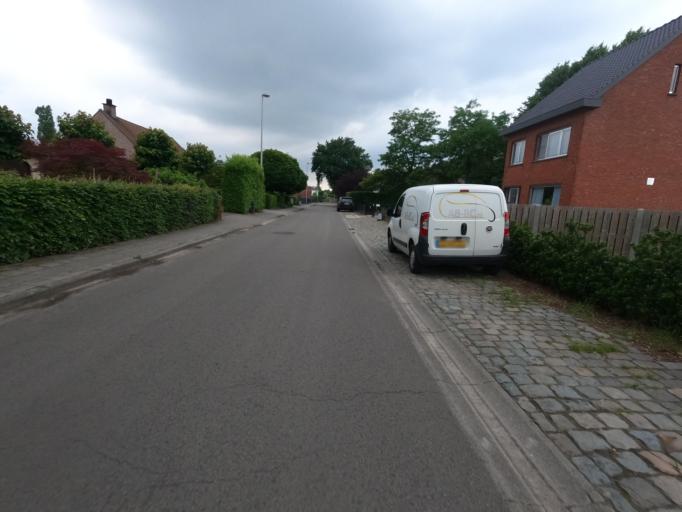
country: BE
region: Flanders
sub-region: Provincie Antwerpen
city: Essen
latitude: 51.4717
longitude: 4.4957
